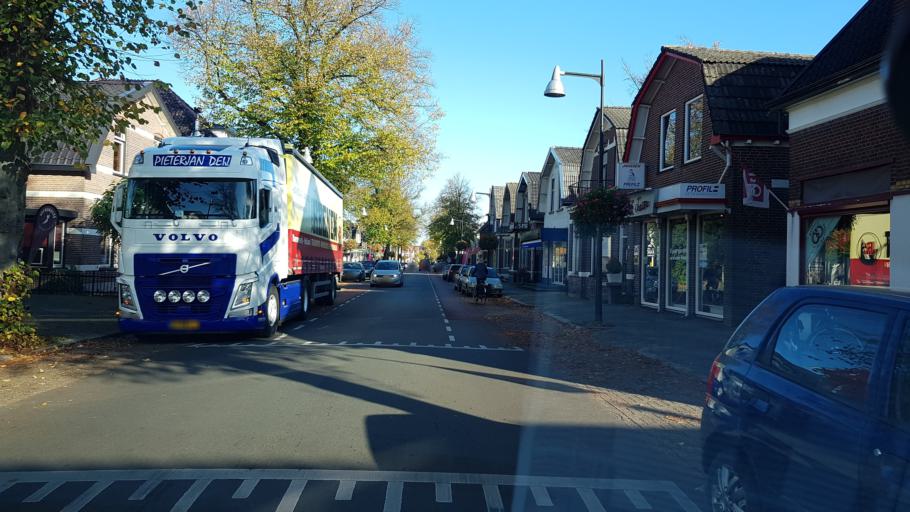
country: NL
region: Gelderland
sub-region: Gemeente Apeldoorn
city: Apeldoorn
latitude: 52.2253
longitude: 5.9568
